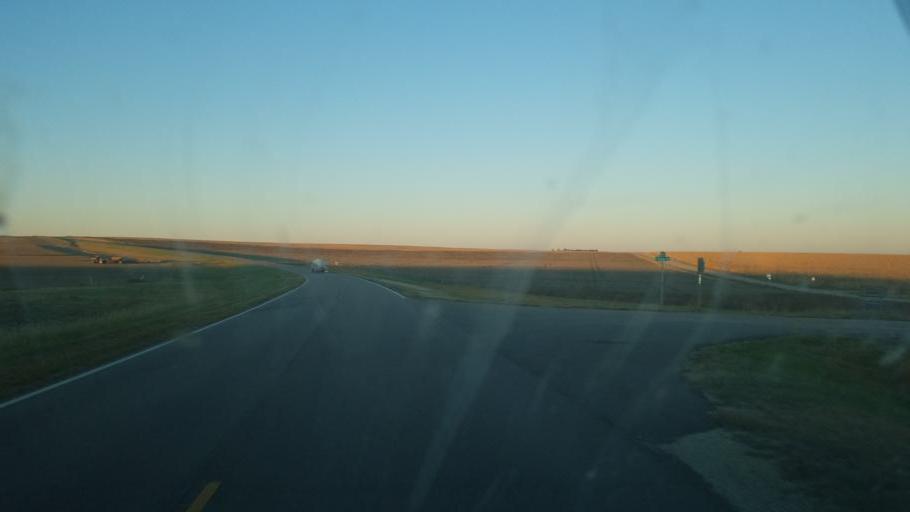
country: US
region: Kansas
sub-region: Wallace County
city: Sharon Springs
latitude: 38.9008
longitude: -101.8592
